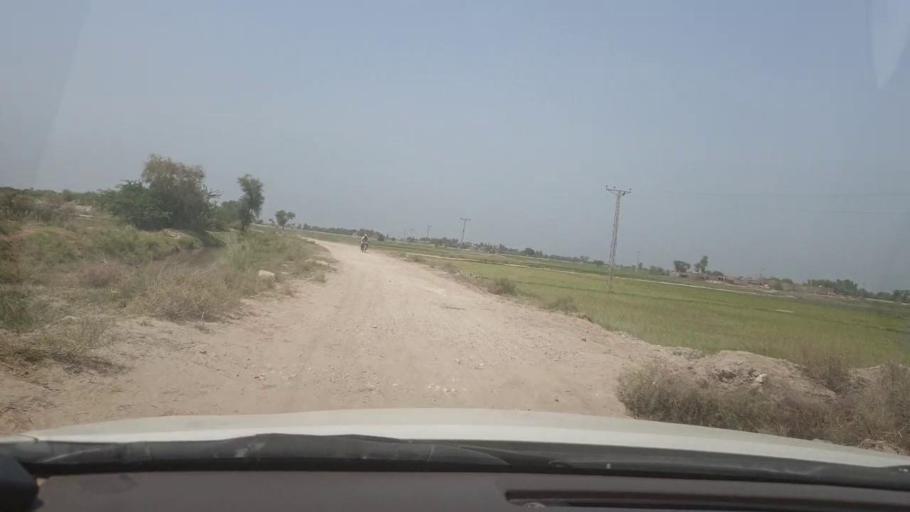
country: PK
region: Sindh
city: Shikarpur
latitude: 27.9386
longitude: 68.5750
